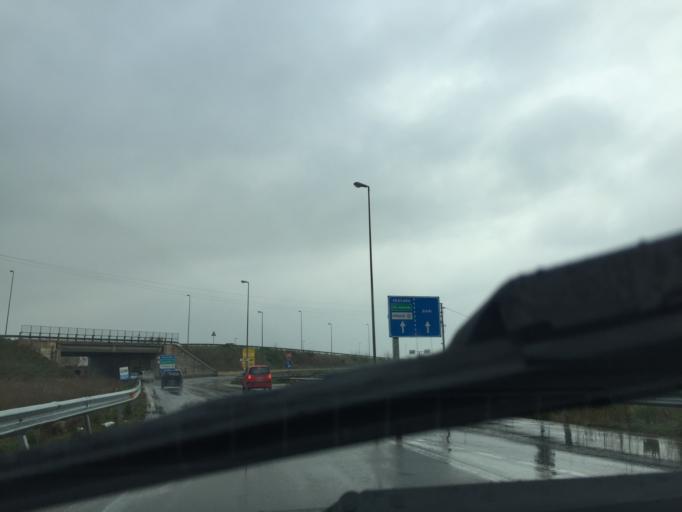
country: IT
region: Apulia
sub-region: Provincia di Foggia
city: Foggia
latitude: 41.4715
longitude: 15.5069
